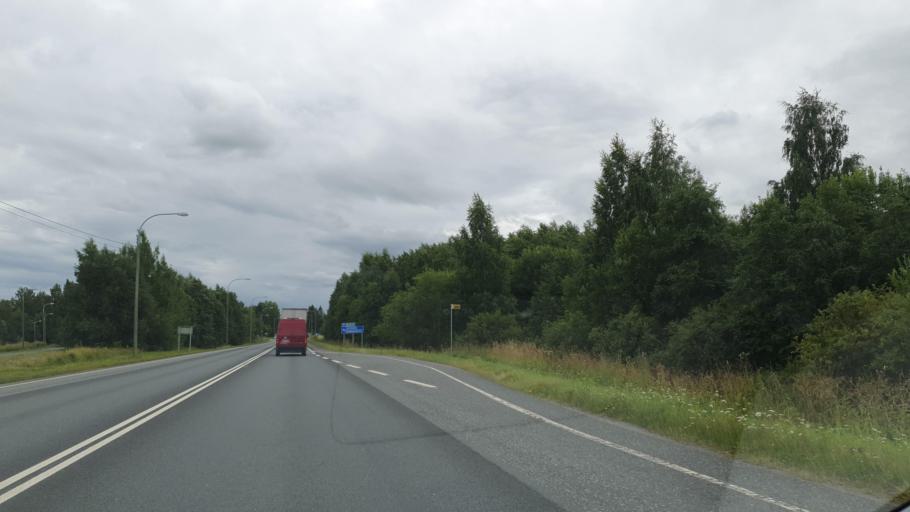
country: FI
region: Northern Savo
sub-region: Ylae-Savo
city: Lapinlahti
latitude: 63.4596
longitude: 27.3132
